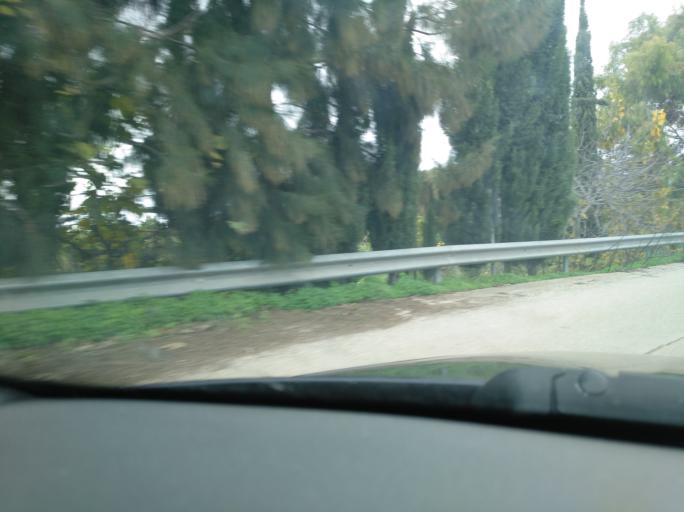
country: PT
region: Faro
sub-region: Vila Real de Santo Antonio
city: Monte Gordo
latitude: 37.1988
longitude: -7.4843
